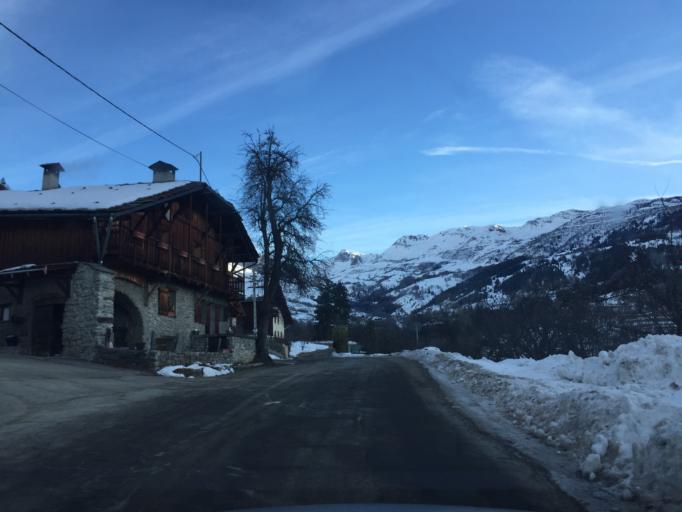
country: FR
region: Rhone-Alpes
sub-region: Departement de la Savoie
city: Aigueblanche
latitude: 45.5505
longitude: 6.5029
